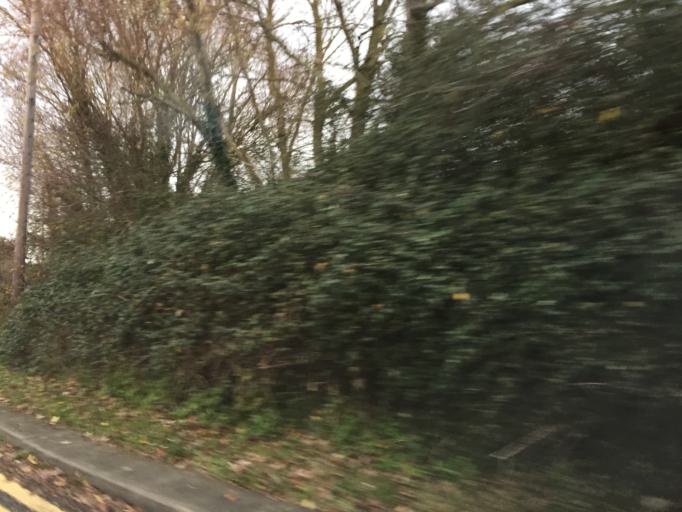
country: GB
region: Wales
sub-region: Newport
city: Bishton
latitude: 51.5744
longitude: -2.8633
